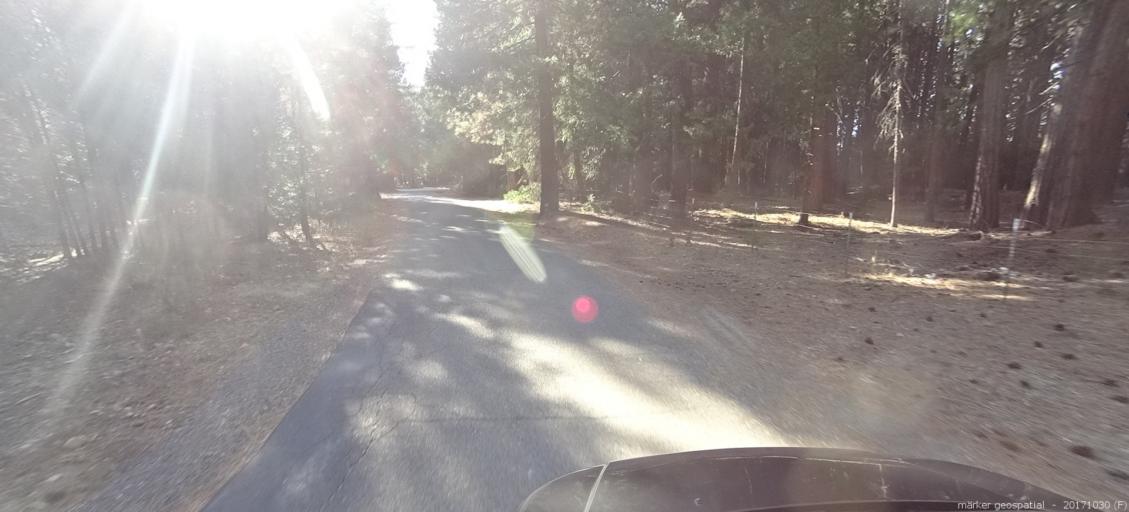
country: US
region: California
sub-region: Shasta County
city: Shingletown
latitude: 40.5379
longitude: -121.7297
